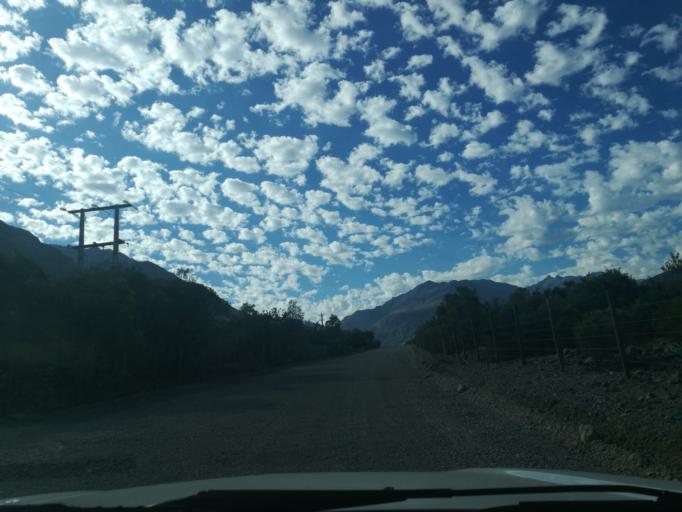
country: CL
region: O'Higgins
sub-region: Provincia de Cachapoal
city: Machali
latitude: -34.2963
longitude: -70.4300
